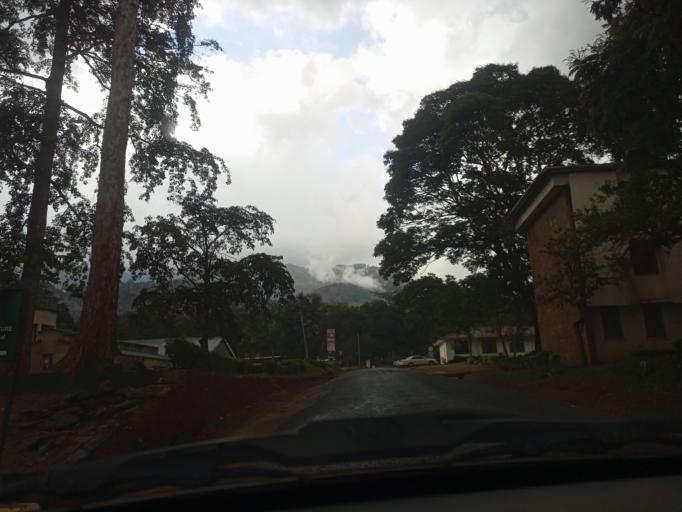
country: TZ
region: Morogoro
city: Morogoro
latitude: -6.8527
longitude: 37.6566
